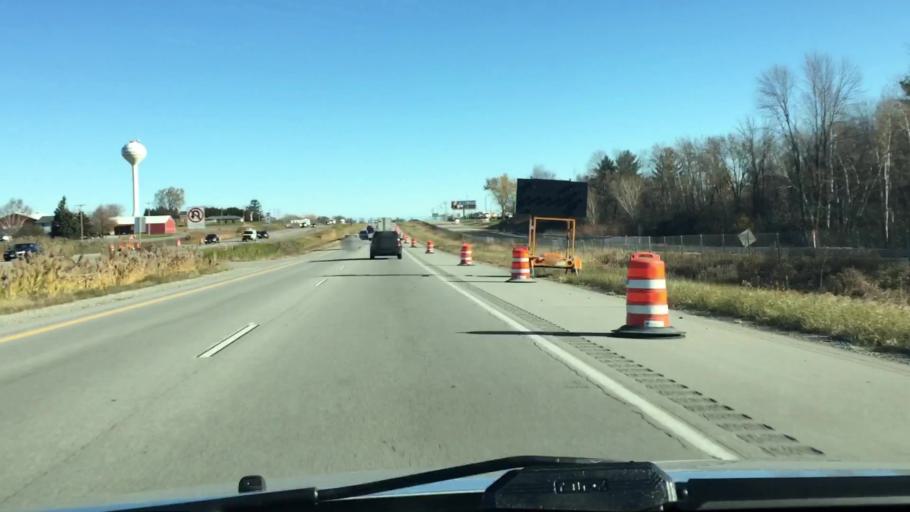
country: US
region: Wisconsin
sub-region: Brown County
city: De Pere
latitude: 44.4119
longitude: -88.1374
